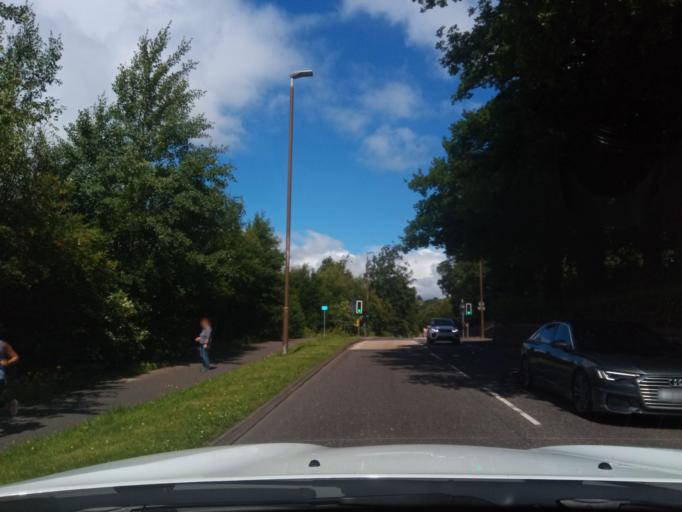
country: GB
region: Scotland
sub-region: Stirling
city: Bridge of Allan
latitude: 56.1408
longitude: -3.9262
